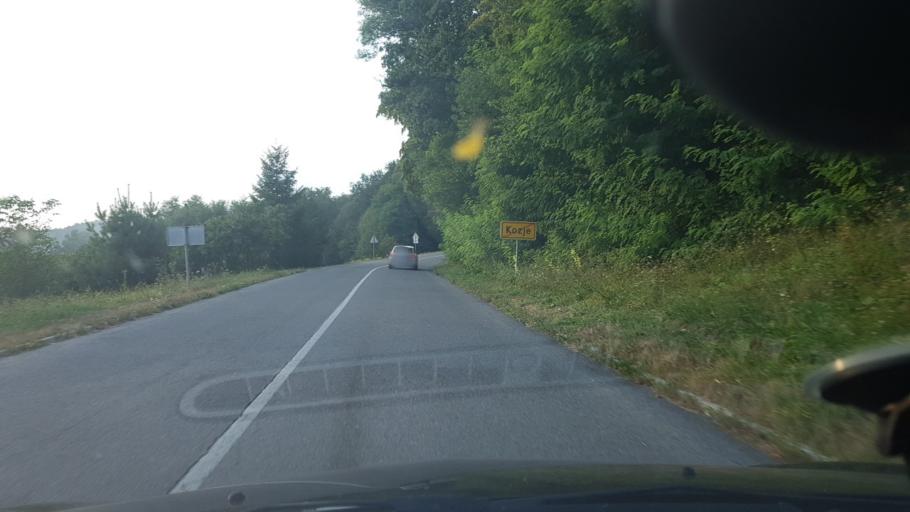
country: SI
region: Kozje
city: Kozje
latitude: 46.0720
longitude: 15.5699
